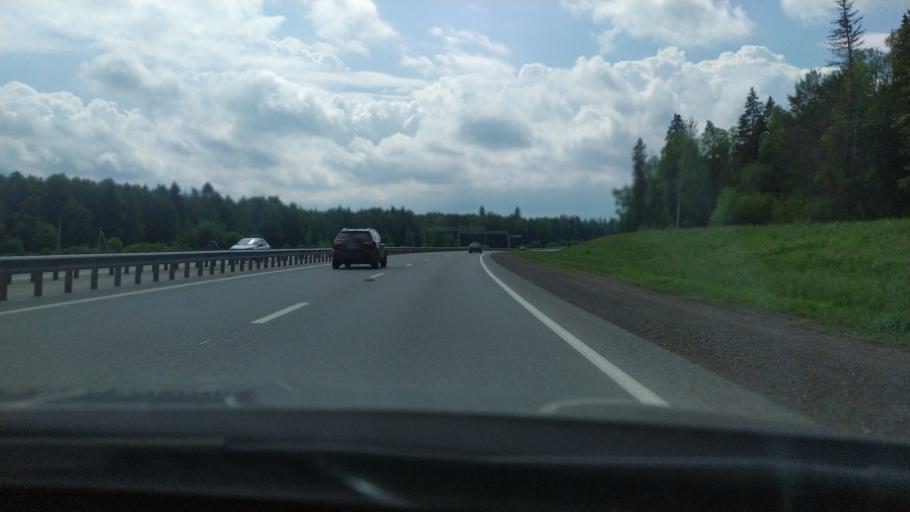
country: RU
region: Perm
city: Novyye Lyady
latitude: 58.0342
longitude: 56.4341
